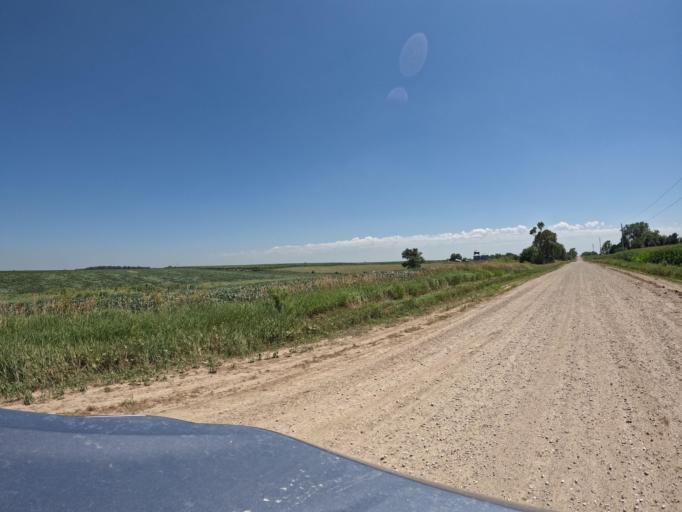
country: US
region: Iowa
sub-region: Poweshiek County
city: Montezuma
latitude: 41.4749
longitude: -92.3936
